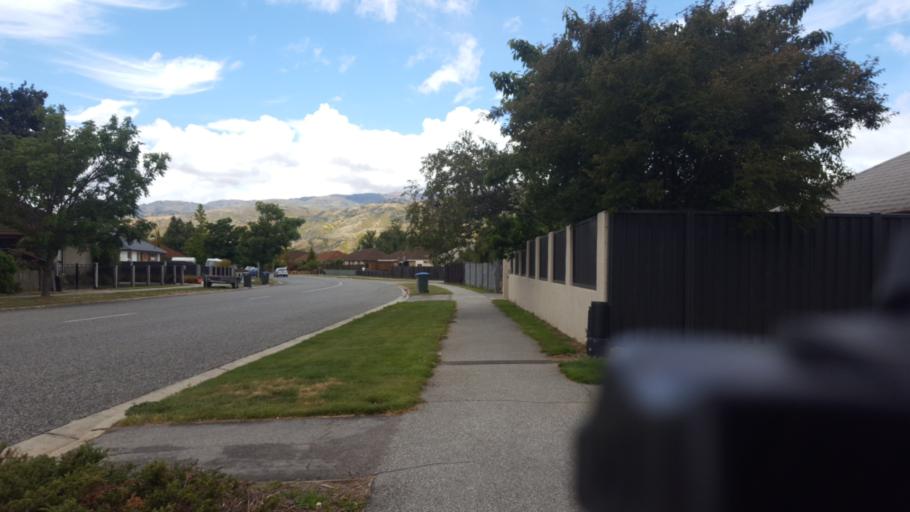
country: NZ
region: Otago
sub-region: Queenstown-Lakes District
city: Wanaka
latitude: -45.0396
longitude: 169.1879
